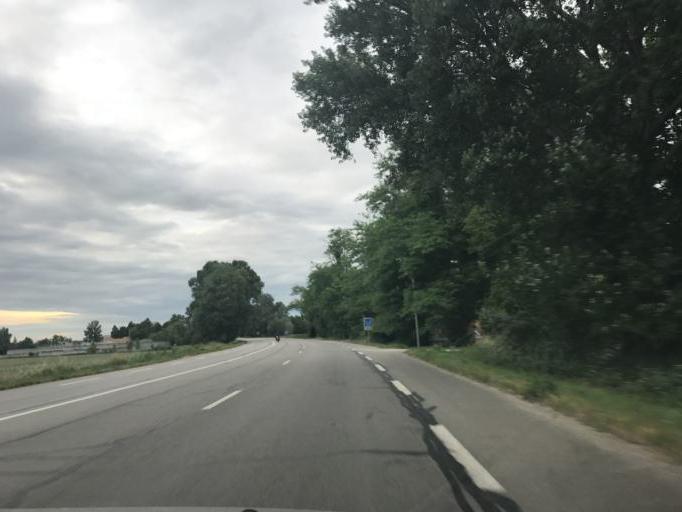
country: FR
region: Rhone-Alpes
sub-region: Departement de la Drome
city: Portes-les-Valence
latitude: 44.8668
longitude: 4.8614
